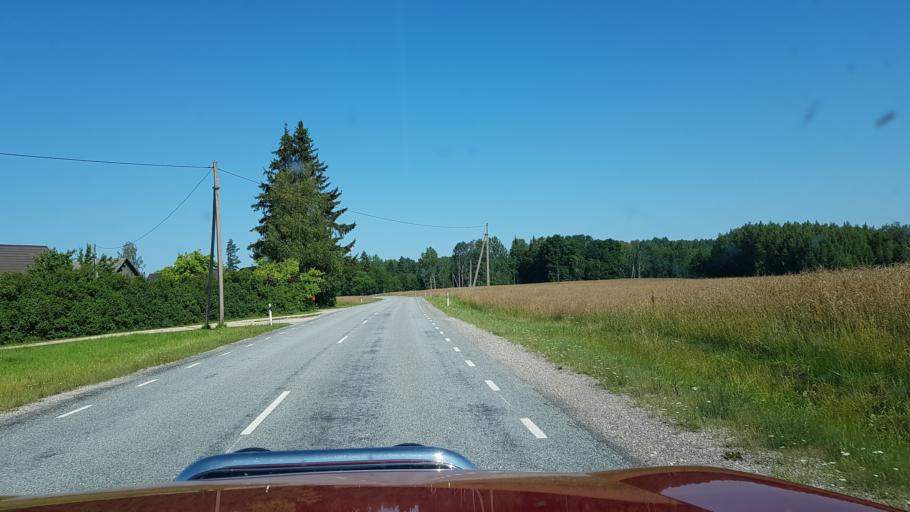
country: EE
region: Polvamaa
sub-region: Polva linn
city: Polva
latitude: 58.0832
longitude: 26.8339
